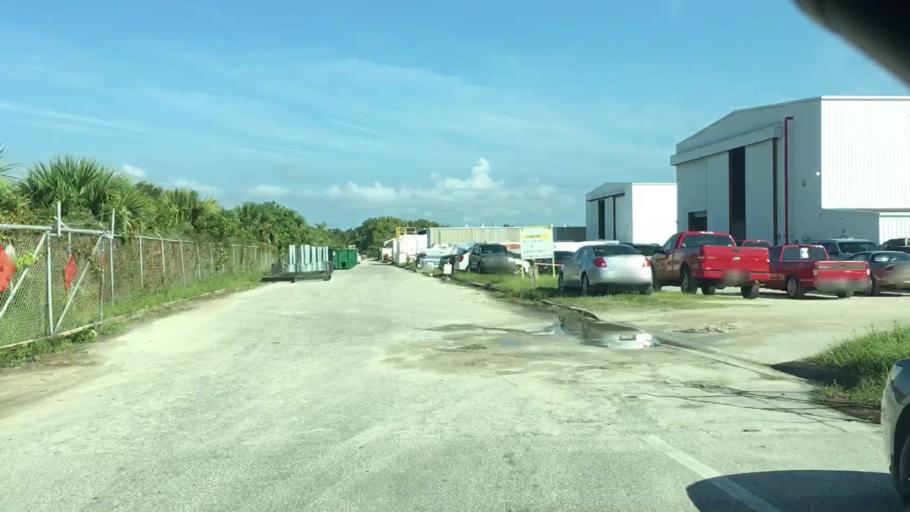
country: US
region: Florida
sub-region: Brevard County
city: Titusville
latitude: 28.6227
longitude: -80.8138
